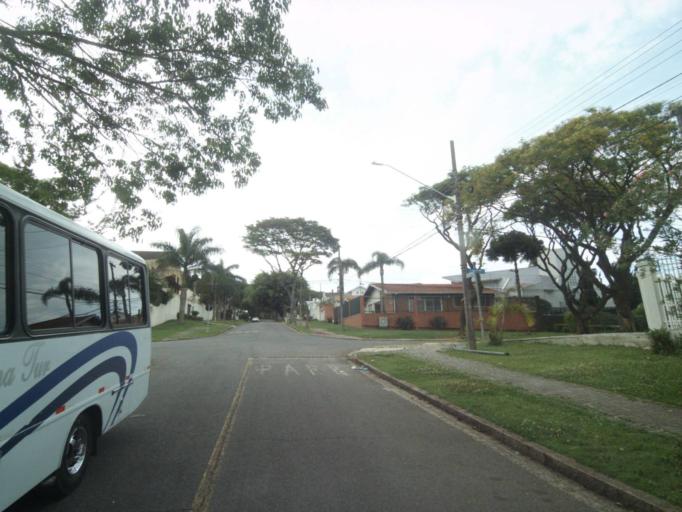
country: BR
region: Parana
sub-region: Curitiba
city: Curitiba
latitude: -25.4265
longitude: -49.2369
